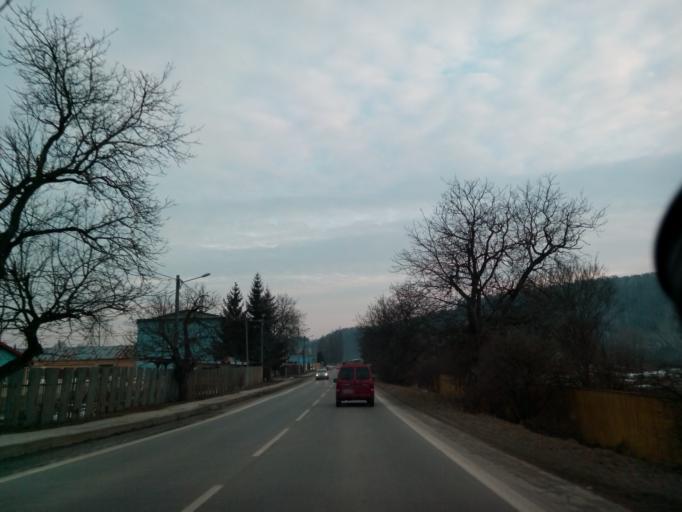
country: SK
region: Presovsky
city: Sabinov
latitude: 49.1104
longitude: 21.0827
